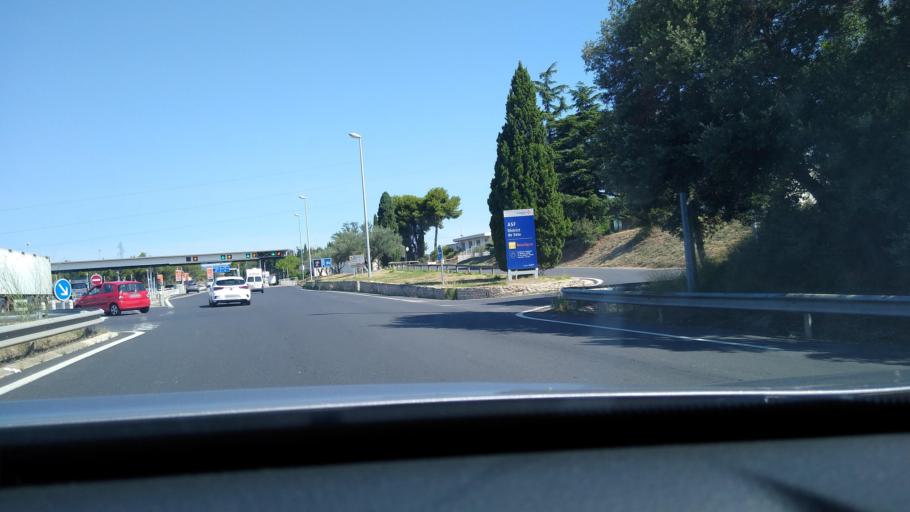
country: FR
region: Languedoc-Roussillon
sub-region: Departement de l'Herault
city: Balaruc-le-Vieux
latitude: 43.4763
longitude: 3.6857
